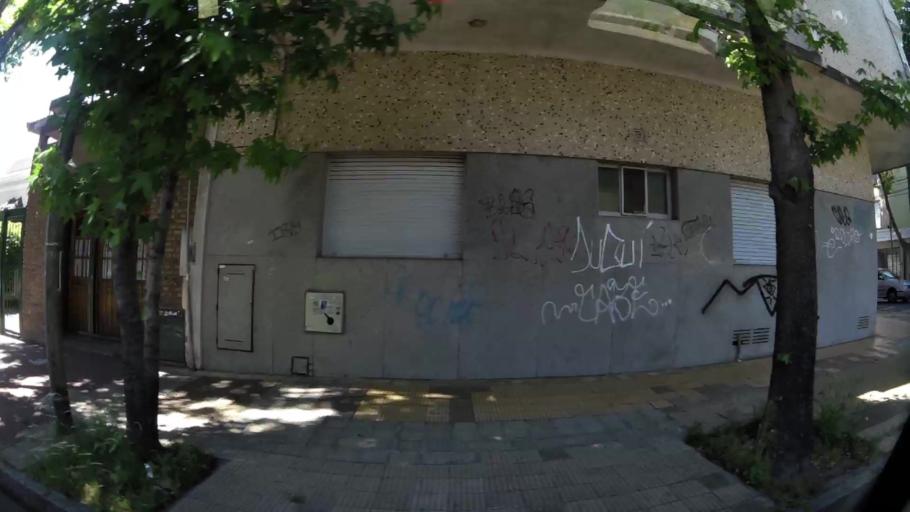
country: AR
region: Buenos Aires
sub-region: Partido de Vicente Lopez
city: Olivos
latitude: -34.5168
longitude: -58.4900
